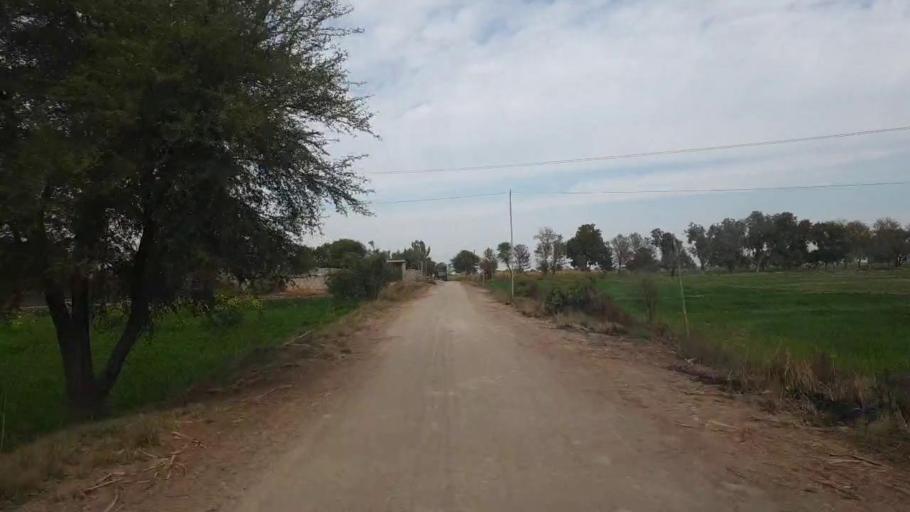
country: PK
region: Sindh
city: Sanghar
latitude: 26.0400
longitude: 68.9113
